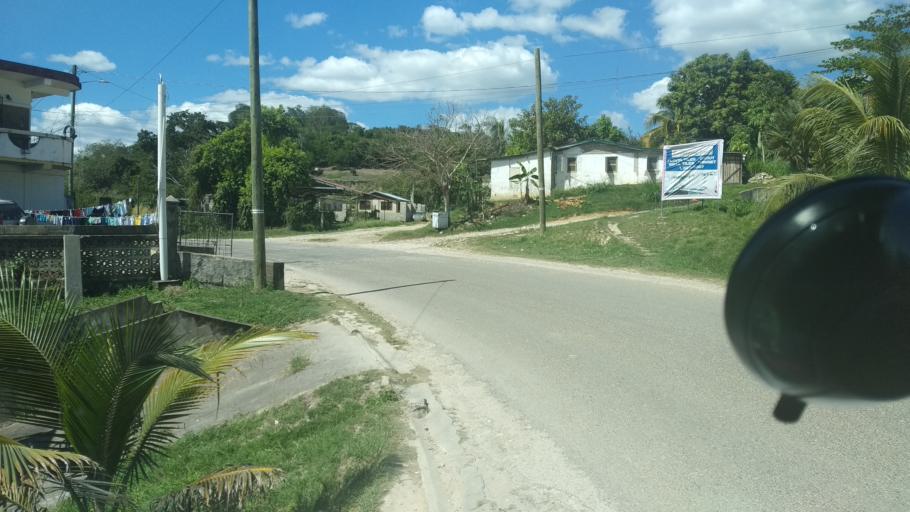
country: BZ
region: Cayo
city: Benque Viejo del Carmen
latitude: 17.0762
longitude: -89.1340
